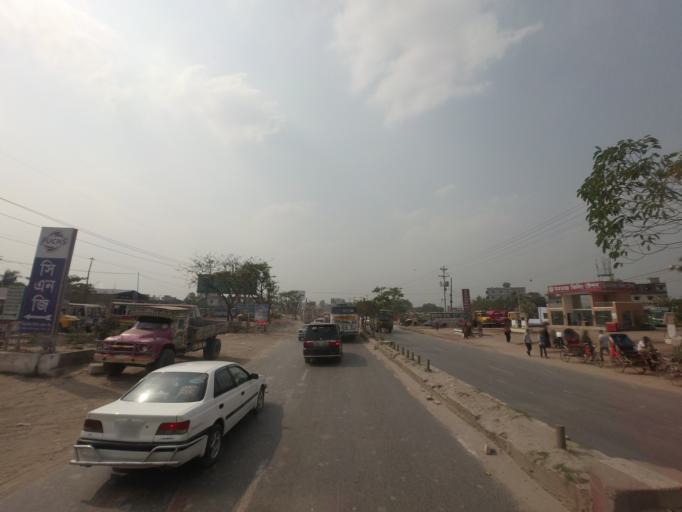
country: BD
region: Dhaka
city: Azimpur
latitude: 23.7880
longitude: 90.3272
